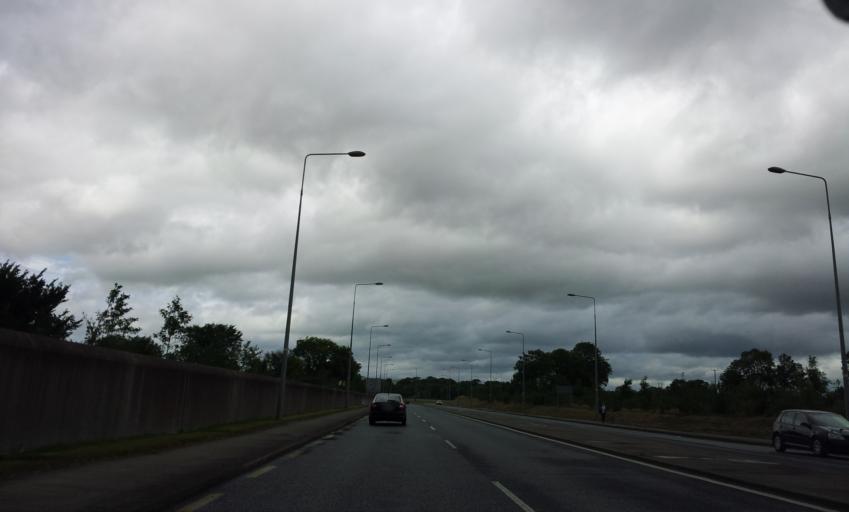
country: IE
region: Munster
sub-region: Waterford
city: Waterford
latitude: 52.2737
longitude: -7.1329
